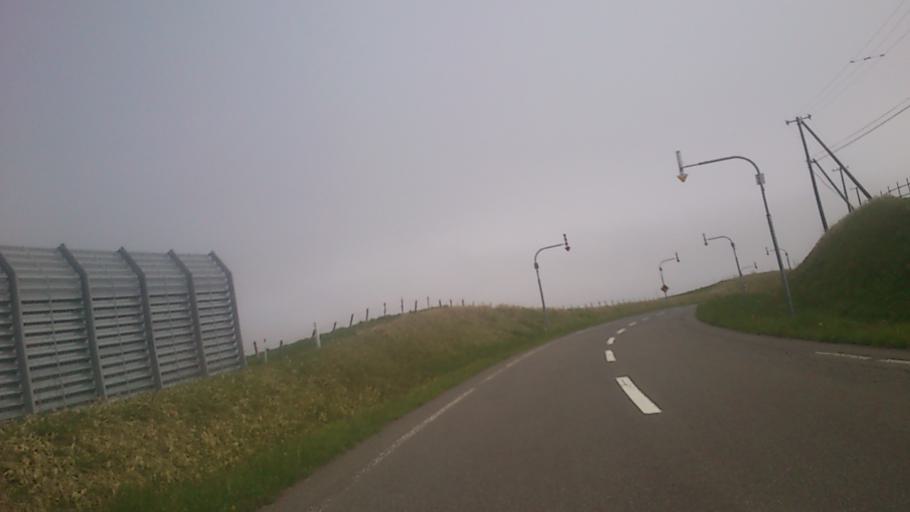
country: JP
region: Hokkaido
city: Nemuro
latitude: 43.1823
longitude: 145.3264
